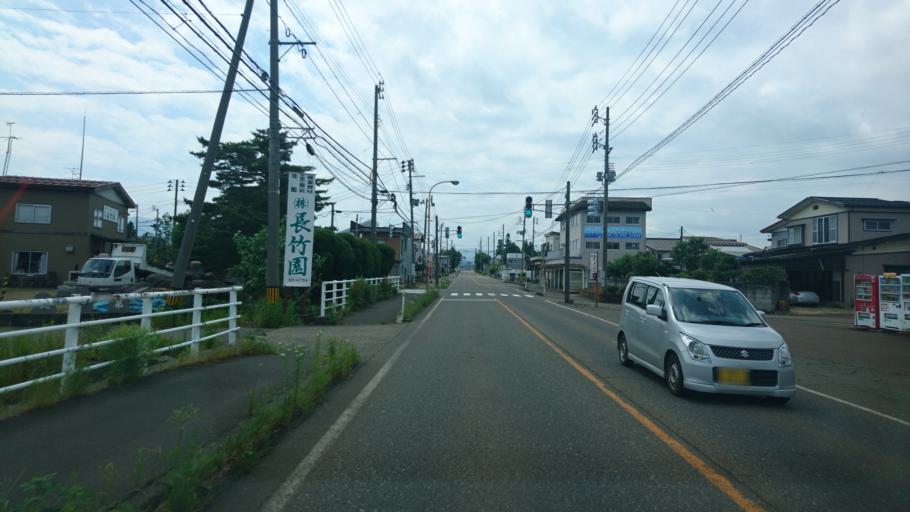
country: JP
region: Niigata
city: Arai
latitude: 37.0706
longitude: 138.2571
